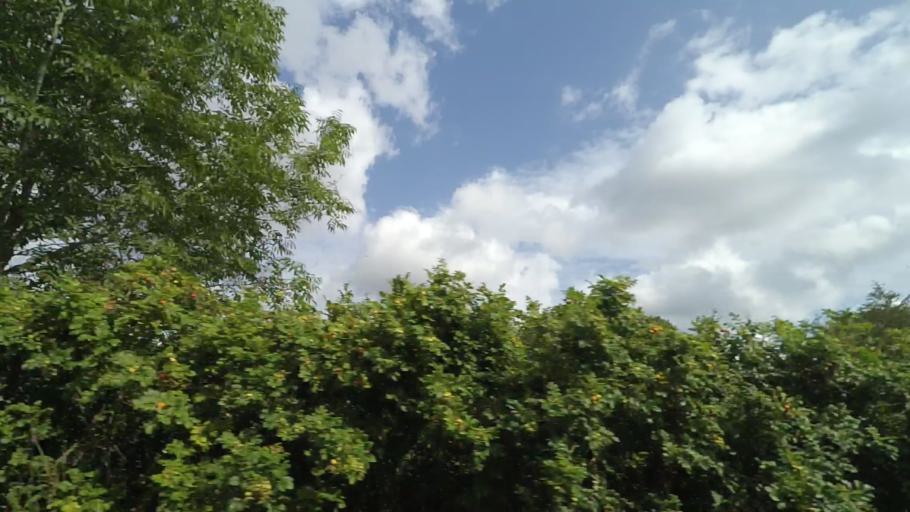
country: DK
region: Central Jutland
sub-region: Syddjurs Kommune
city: Ryomgard
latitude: 56.4832
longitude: 10.4756
